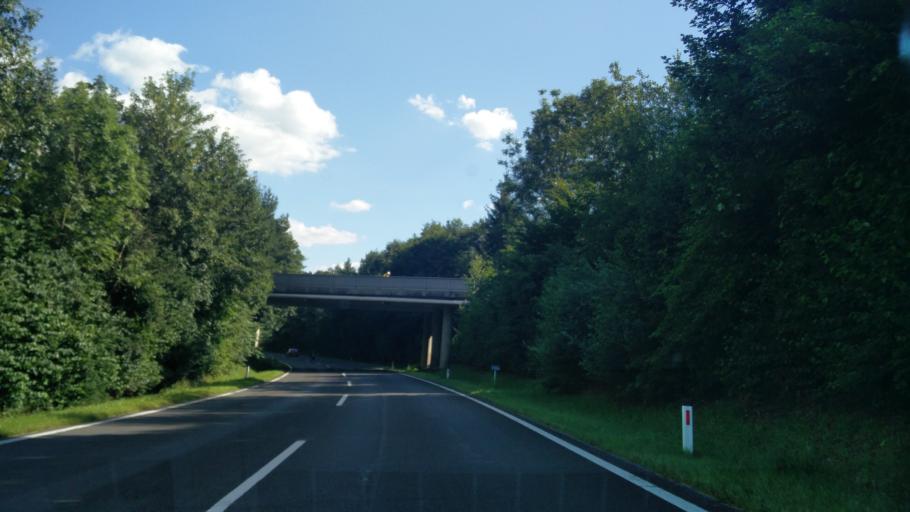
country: AT
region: Styria
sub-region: Politischer Bezirk Leoben
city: Trofaiach
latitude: 47.4245
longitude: 14.9996
